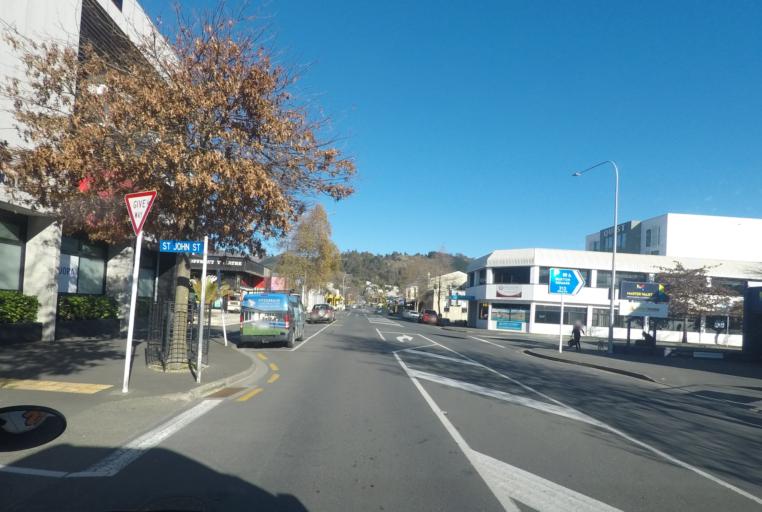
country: NZ
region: Nelson
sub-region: Nelson City
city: Nelson
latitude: -41.2735
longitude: 173.2870
